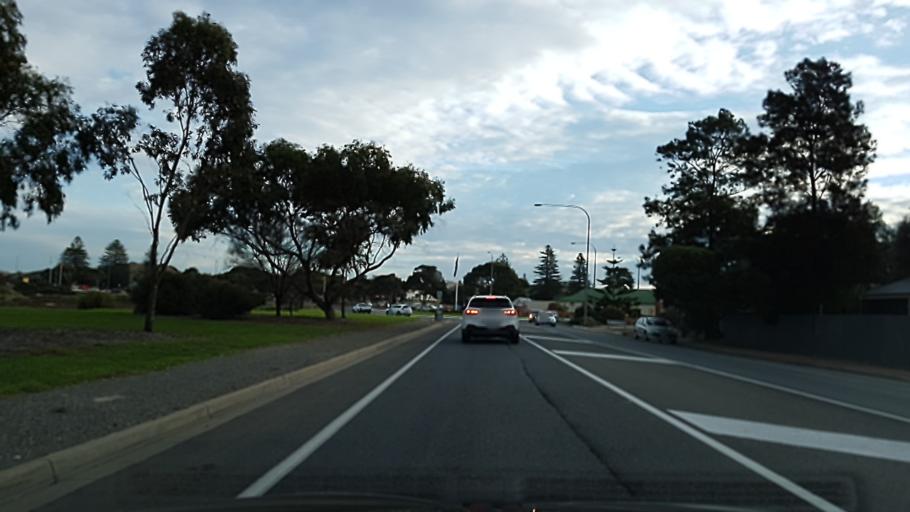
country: AU
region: South Australia
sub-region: Adelaide
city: Port Noarlunga
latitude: -35.1486
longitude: 138.4741
